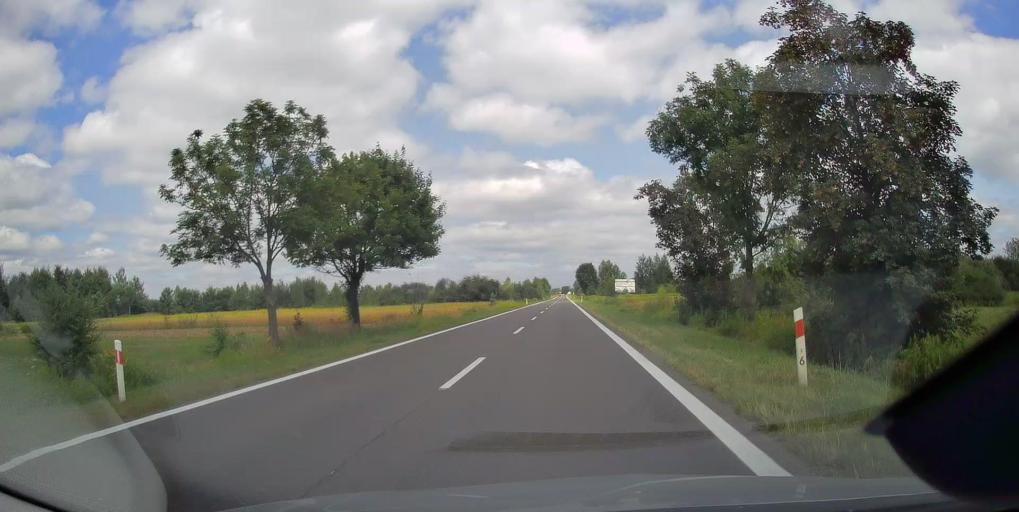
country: PL
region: Subcarpathian Voivodeship
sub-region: Powiat tarnobrzeski
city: Baranow Sandomierski
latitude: 50.4944
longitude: 21.5701
